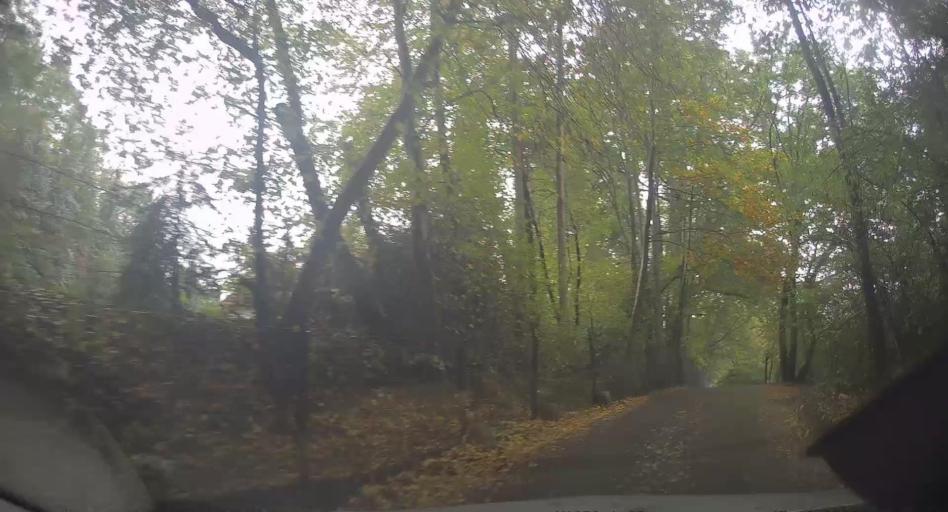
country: PL
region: Lesser Poland Voivodeship
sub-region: Powiat krakowski
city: Ochojno
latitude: 49.9922
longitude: 19.9890
